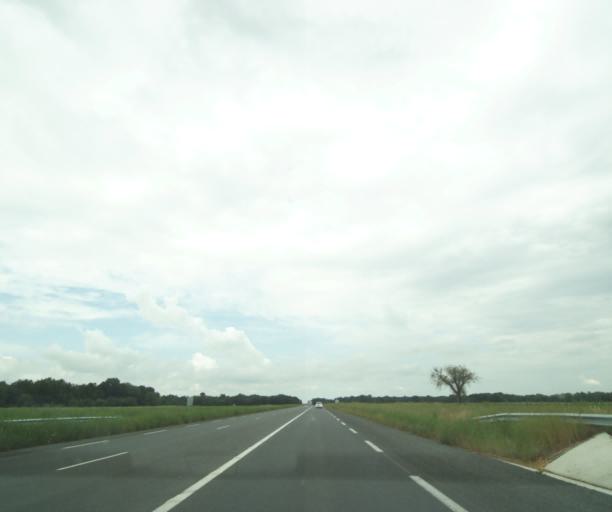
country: FR
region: Poitou-Charentes
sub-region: Departement des Deux-Sevres
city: Sainte-Verge
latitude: 47.0289
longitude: -0.2014
